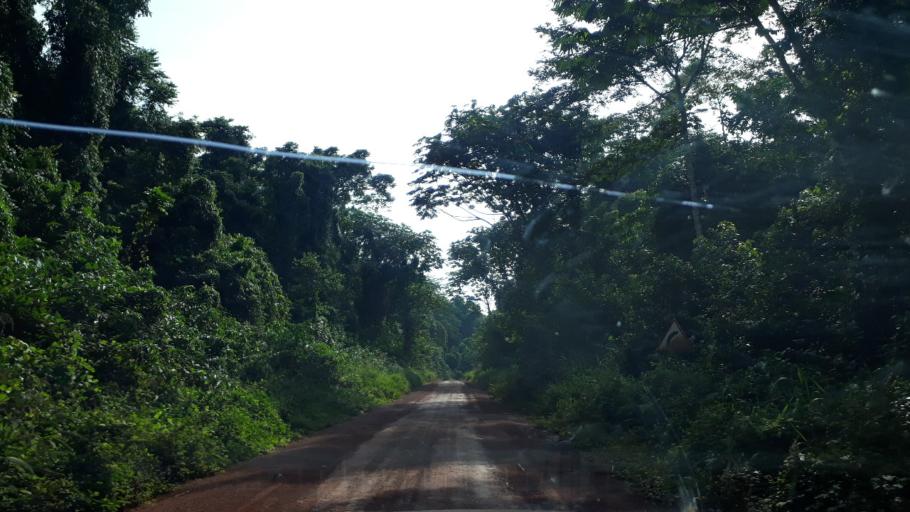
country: CD
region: Eastern Province
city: Wamba
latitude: 1.4200
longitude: 27.7914
